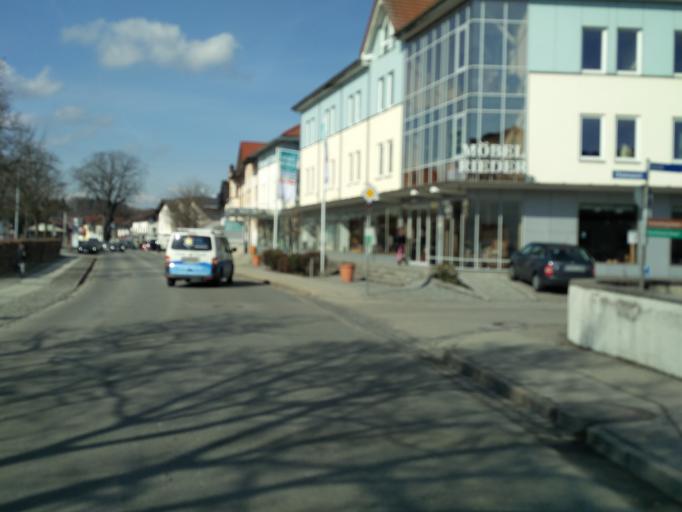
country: DE
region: Bavaria
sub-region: Upper Bavaria
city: Bad Endorf
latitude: 47.9044
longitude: 12.3033
